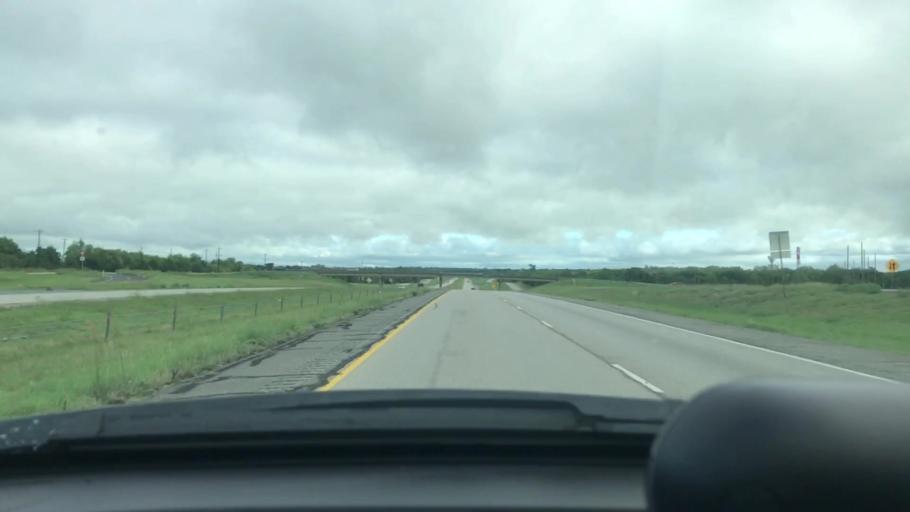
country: US
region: Texas
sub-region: Grayson County
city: Van Alstyne
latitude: 33.3792
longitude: -96.5808
